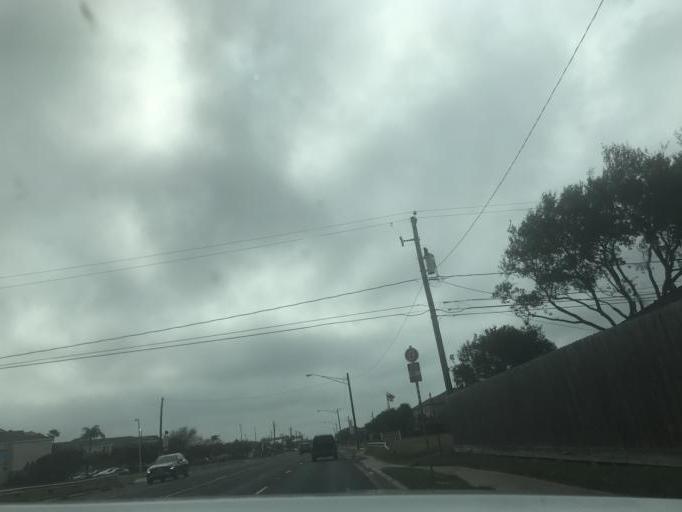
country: US
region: Texas
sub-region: Nueces County
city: Corpus Christi
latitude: 27.6819
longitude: -97.3676
